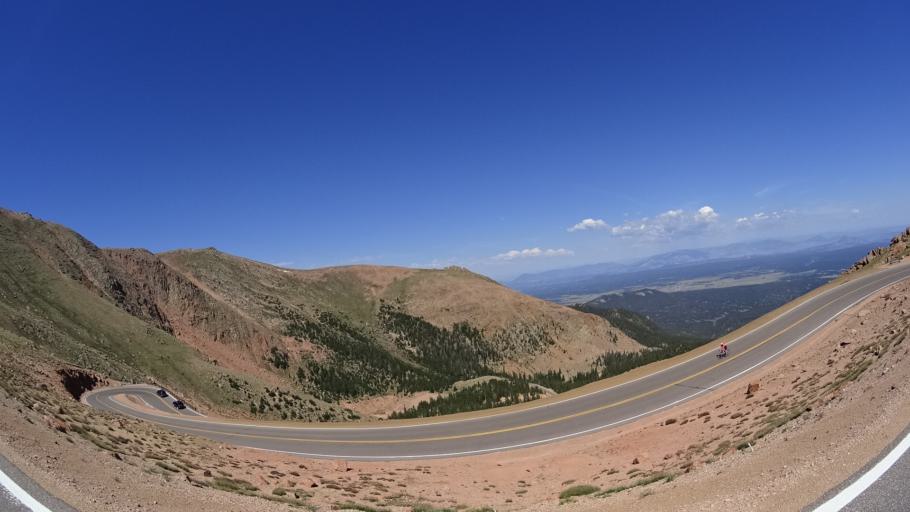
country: US
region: Colorado
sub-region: El Paso County
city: Cascade-Chipita Park
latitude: 38.8702
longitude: -105.0661
